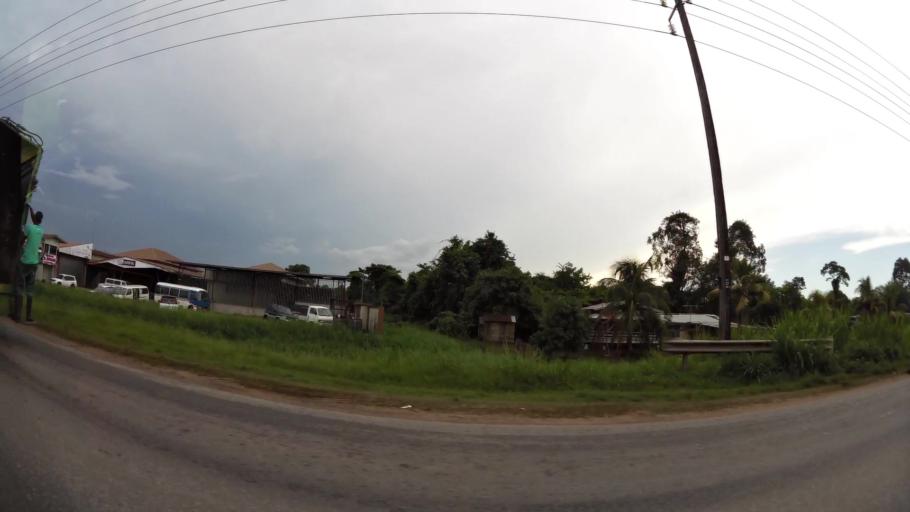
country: SR
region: Paramaribo
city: Paramaribo
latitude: 5.7983
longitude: -55.1855
